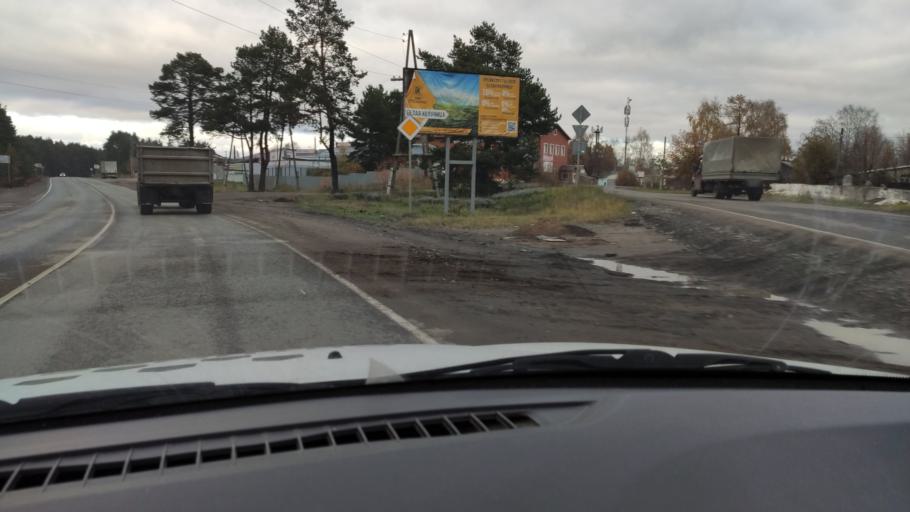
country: RU
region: Kirov
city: Belaya Kholunitsa
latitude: 58.8483
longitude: 50.8265
